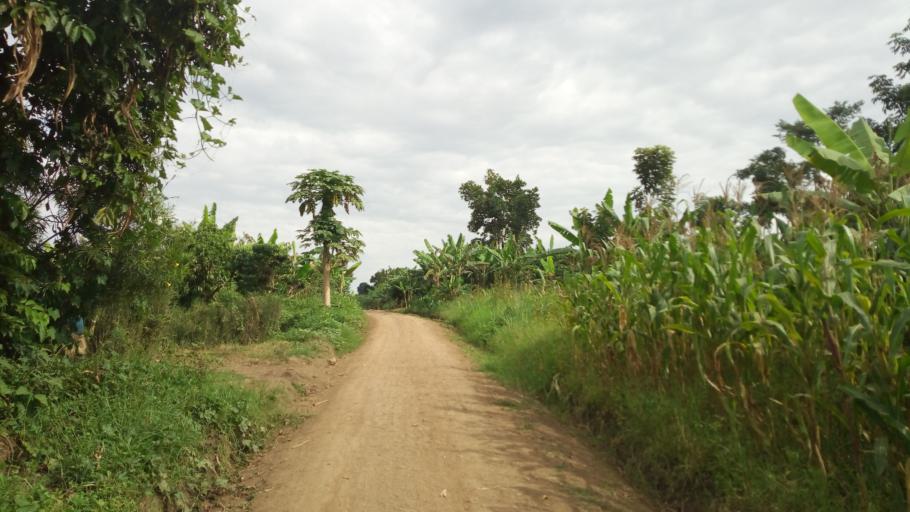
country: UG
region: Central Region
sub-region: Kiboga District
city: Kiboga
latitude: 0.7585
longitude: 31.6996
